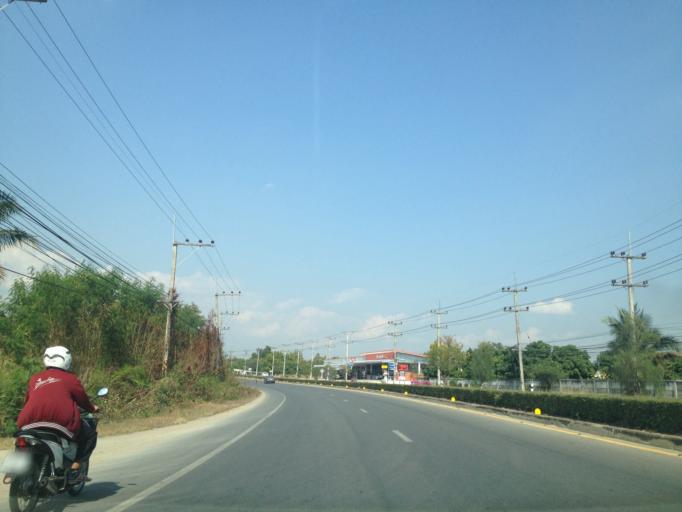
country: TH
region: Chiang Mai
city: San Pa Tong
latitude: 18.5906
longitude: 98.8887
